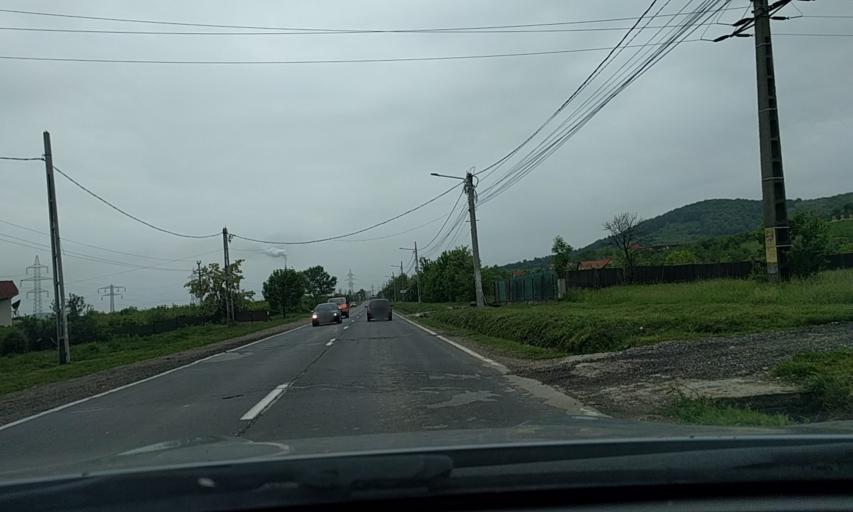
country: RO
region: Dambovita
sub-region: Comuna Aninoasa
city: Sateni
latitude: 44.9769
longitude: 25.4257
